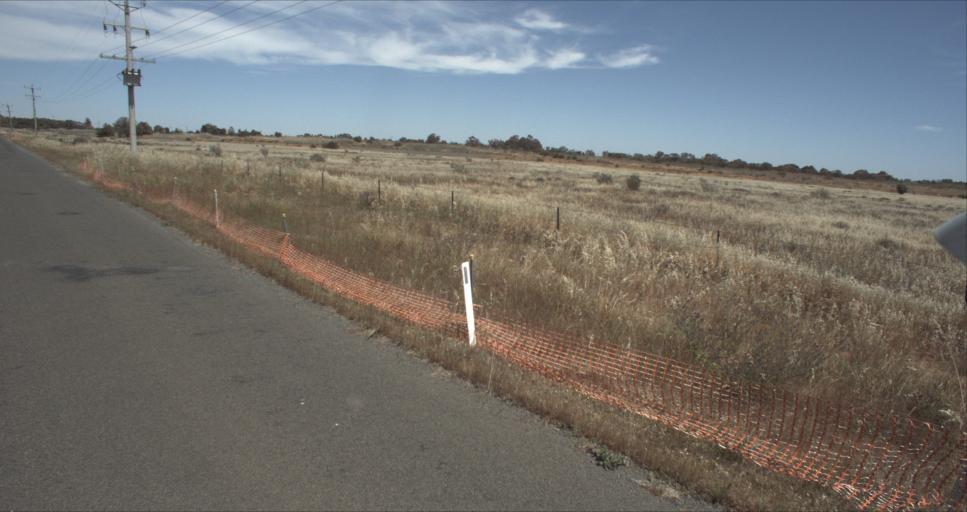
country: AU
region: New South Wales
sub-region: Leeton
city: Leeton
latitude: -34.6049
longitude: 146.4263
